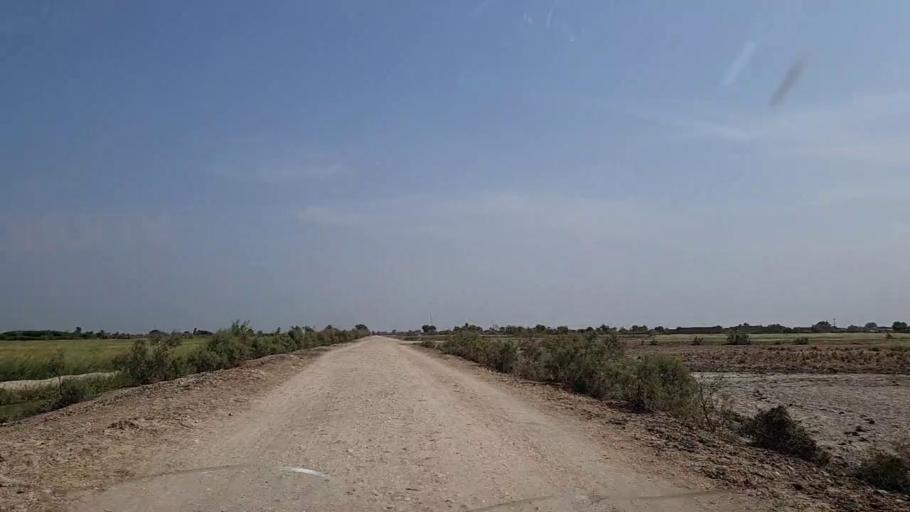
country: PK
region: Sindh
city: Khanpur
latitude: 27.8088
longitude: 69.3093
